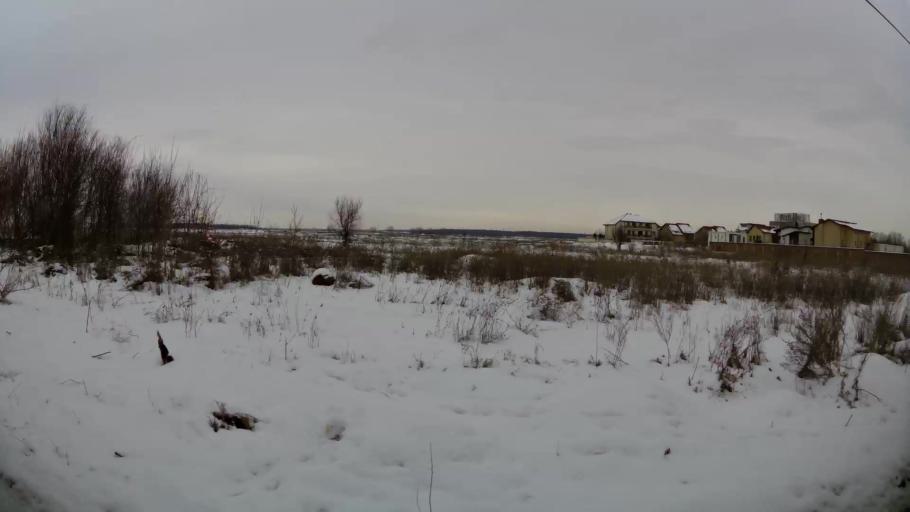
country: RO
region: Ilfov
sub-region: Comuna Tunari
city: Tunari
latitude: 44.5183
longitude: 26.1460
